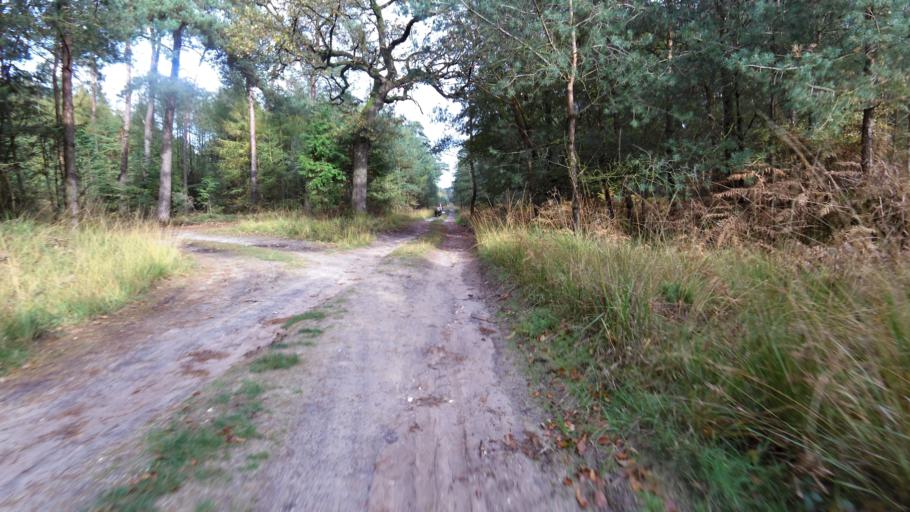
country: NL
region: Gelderland
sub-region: Gemeente Apeldoorn
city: Uddel
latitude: 52.3108
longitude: 5.8536
